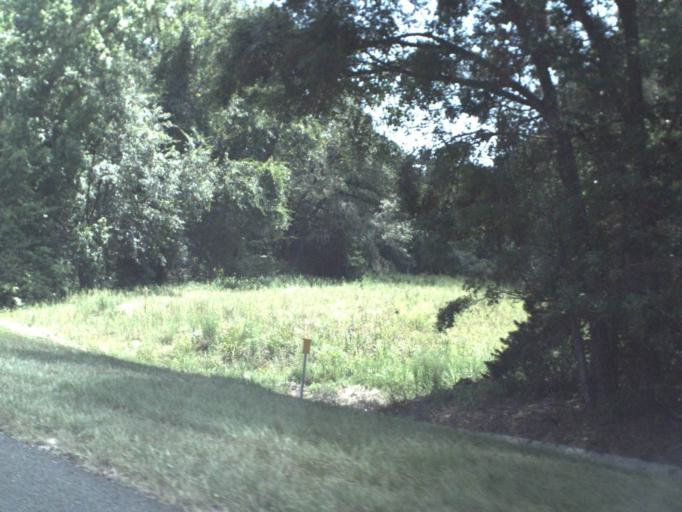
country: US
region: Florida
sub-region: Alachua County
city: Waldo
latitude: 29.7216
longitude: -82.1410
